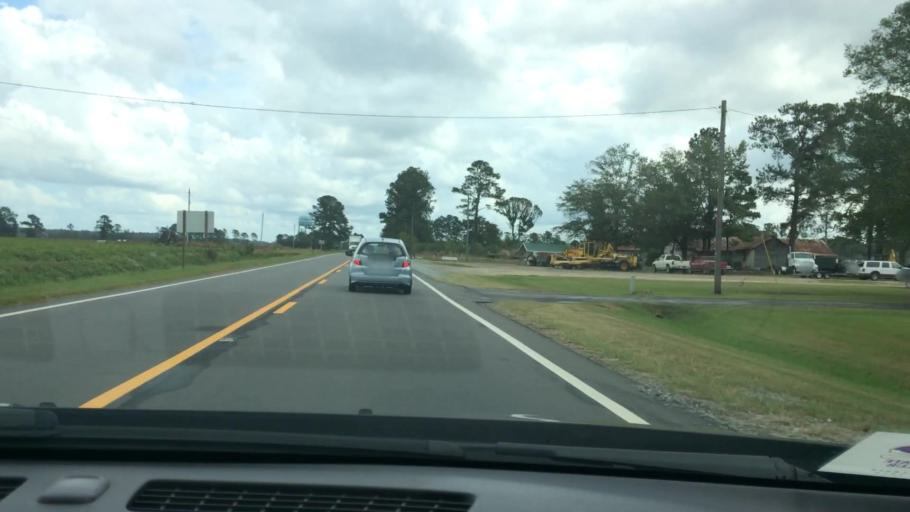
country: US
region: North Carolina
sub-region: Pitt County
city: Farmville
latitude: 35.6025
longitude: -77.6453
